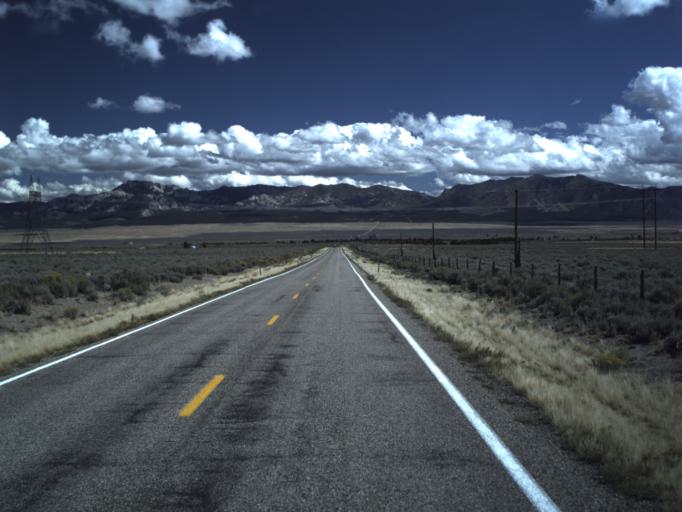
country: US
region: Utah
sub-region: Beaver County
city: Milford
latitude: 38.4105
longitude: -113.0642
